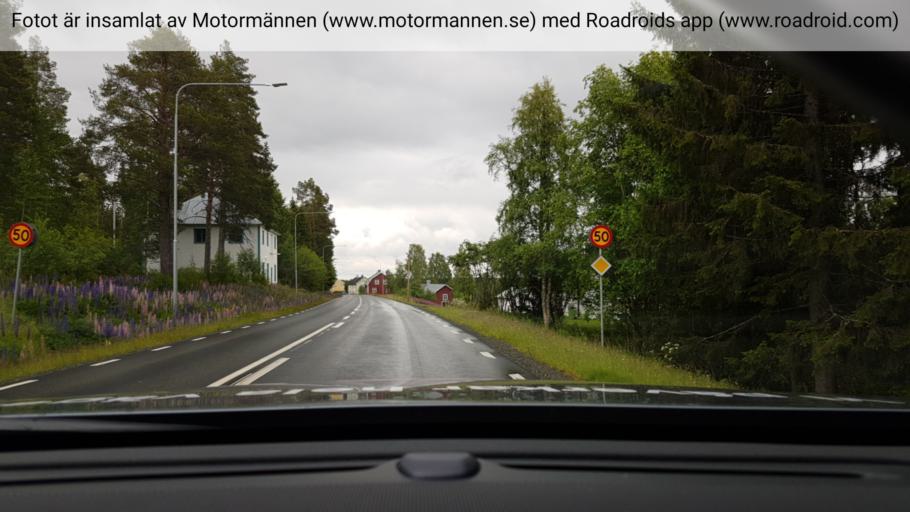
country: SE
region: Vaesterbotten
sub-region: Norsjo Kommun
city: Norsjoe
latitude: 65.2647
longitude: 19.6150
